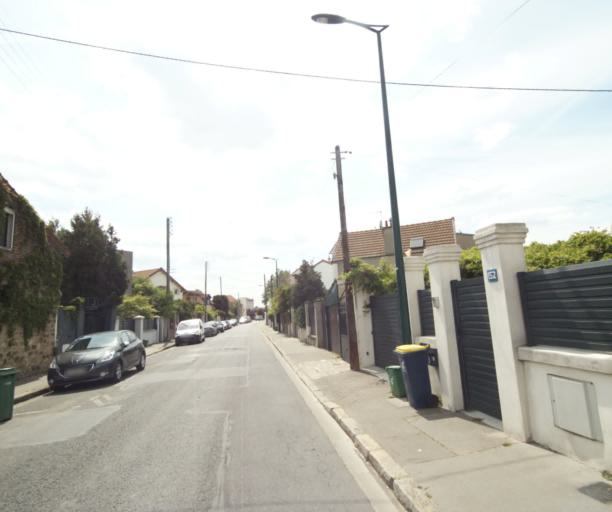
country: FR
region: Ile-de-France
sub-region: Departement des Hauts-de-Seine
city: Colombes
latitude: 48.9181
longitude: 2.2443
